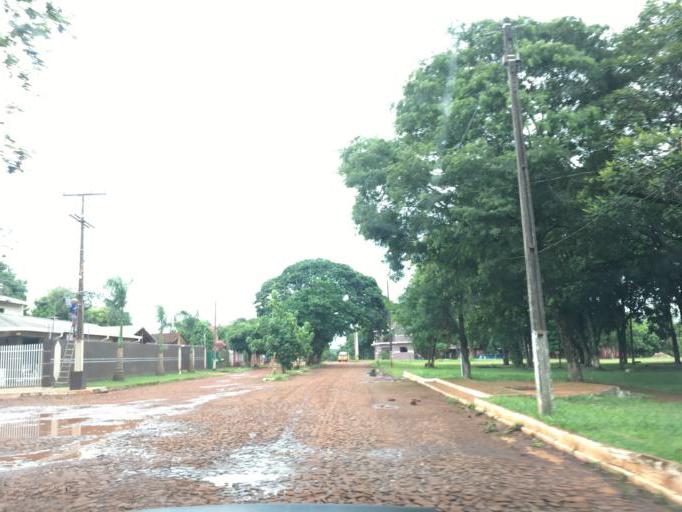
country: PY
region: Alto Parana
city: Ciudad del Este
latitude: -25.4199
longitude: -54.6416
